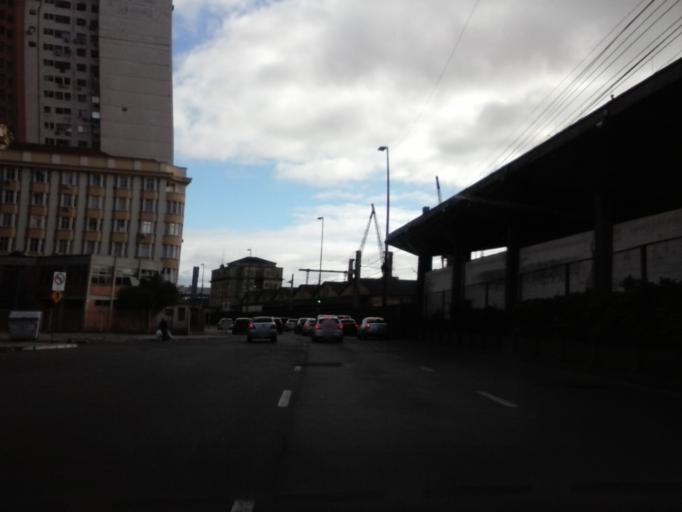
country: BR
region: Rio Grande do Sul
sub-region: Porto Alegre
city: Porto Alegre
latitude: -30.0267
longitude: -51.2284
